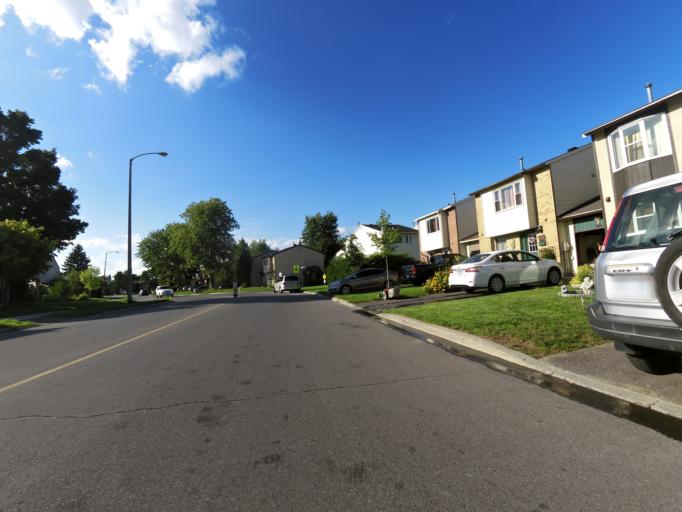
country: CA
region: Quebec
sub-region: Outaouais
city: Gatineau
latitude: 45.4647
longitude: -75.4945
